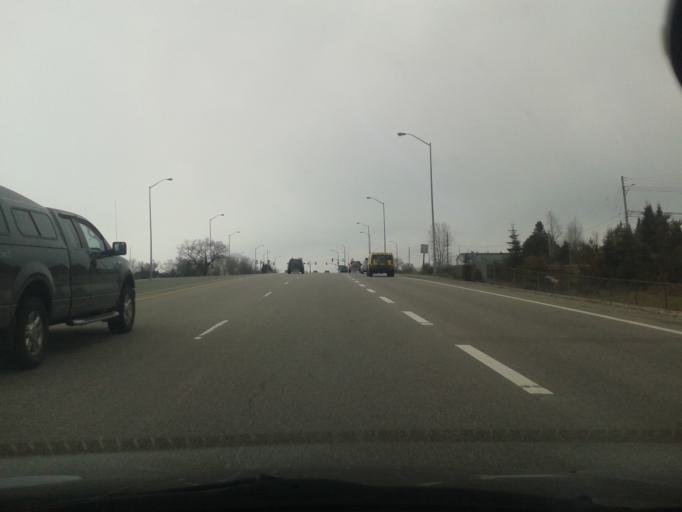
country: CA
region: Ontario
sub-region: Nipissing District
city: North Bay
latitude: 46.3289
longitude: -79.4628
